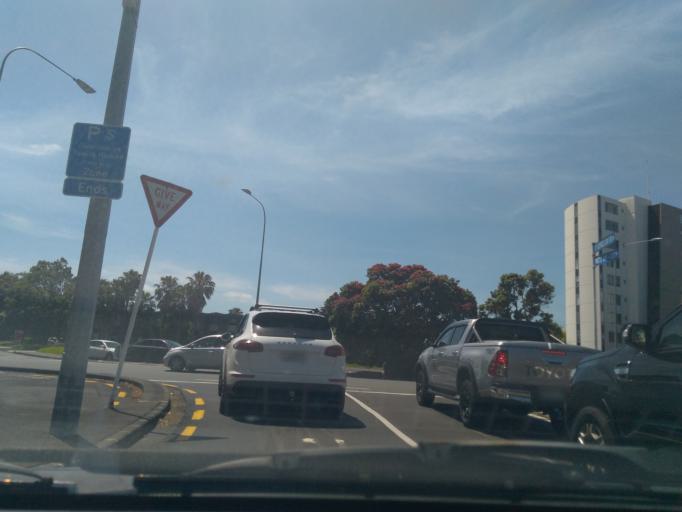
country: NZ
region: Auckland
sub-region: Auckland
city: Auckland
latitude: -36.8503
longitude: 174.7820
